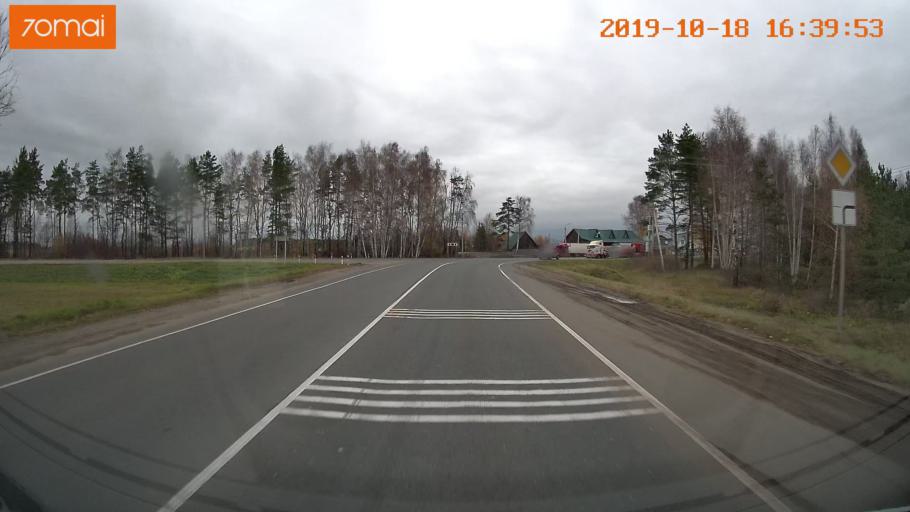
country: RU
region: Vladimir
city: Suzdal'
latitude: 56.4562
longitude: 40.4592
